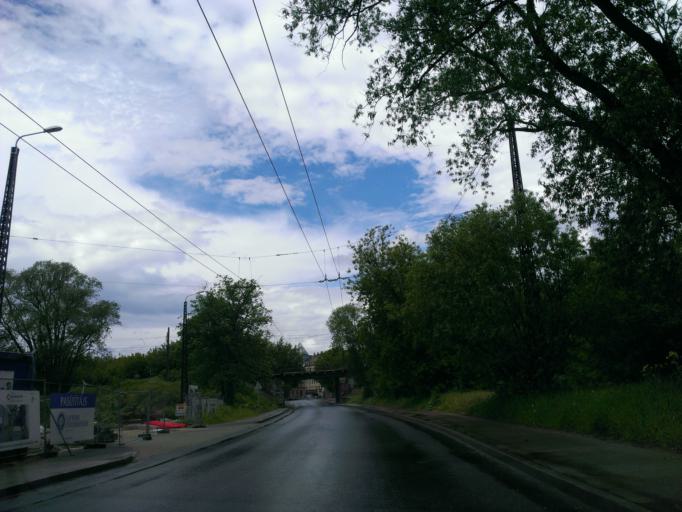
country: LV
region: Riga
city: Riga
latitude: 56.9372
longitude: 24.0979
